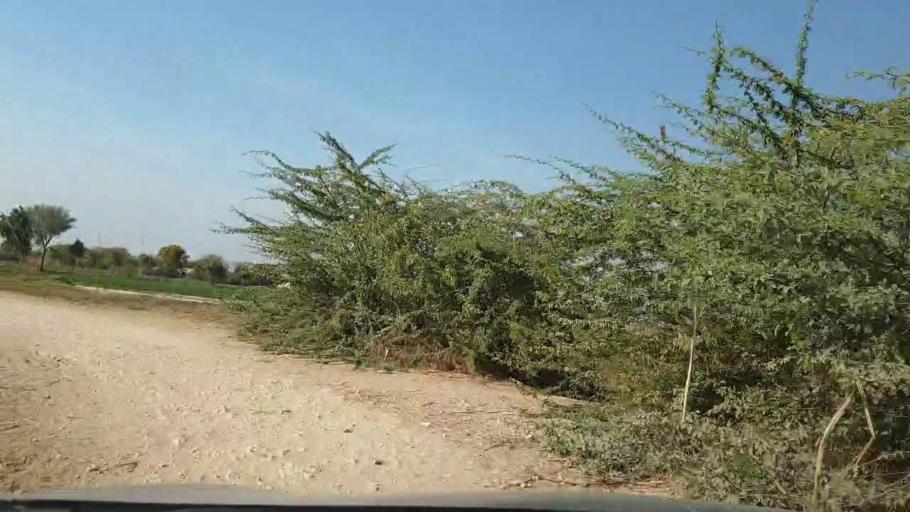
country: PK
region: Sindh
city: Berani
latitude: 25.7211
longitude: 68.7635
